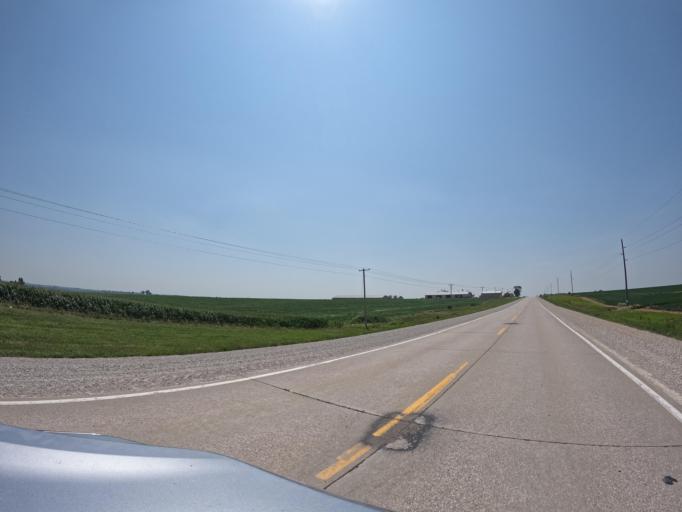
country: US
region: Iowa
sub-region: Keokuk County
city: Sigourney
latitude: 41.3368
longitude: -92.2460
